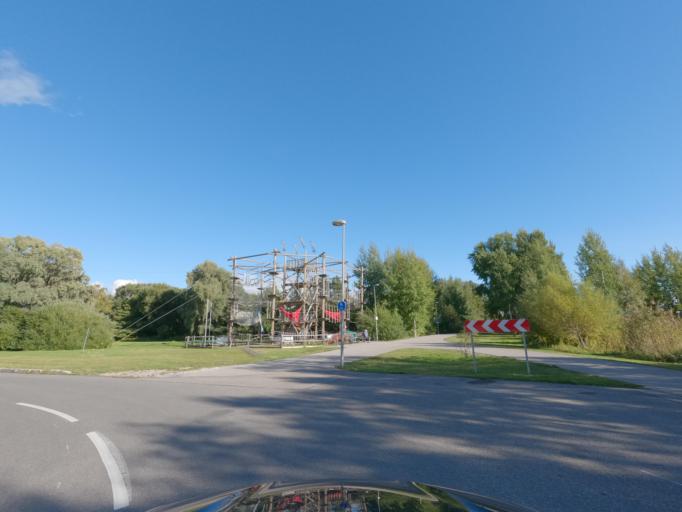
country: EE
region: Paernumaa
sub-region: Paernu linn
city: Parnu
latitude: 58.3736
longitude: 24.5201
